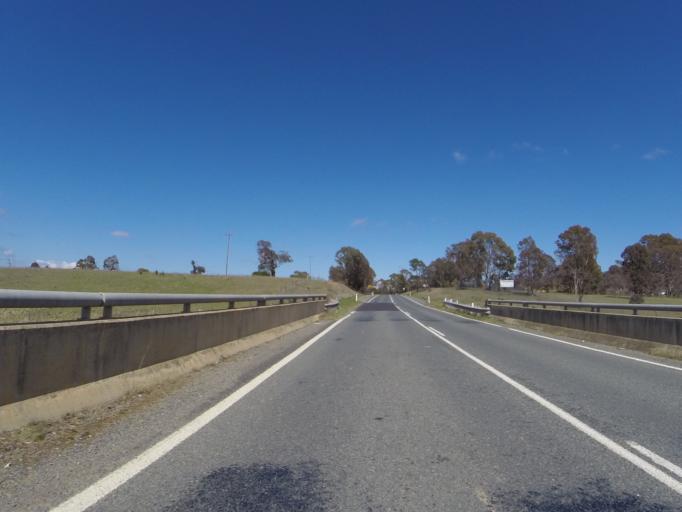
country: AU
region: New South Wales
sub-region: Queanbeyan
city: Queanbeyan
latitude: -35.3208
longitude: 149.2426
